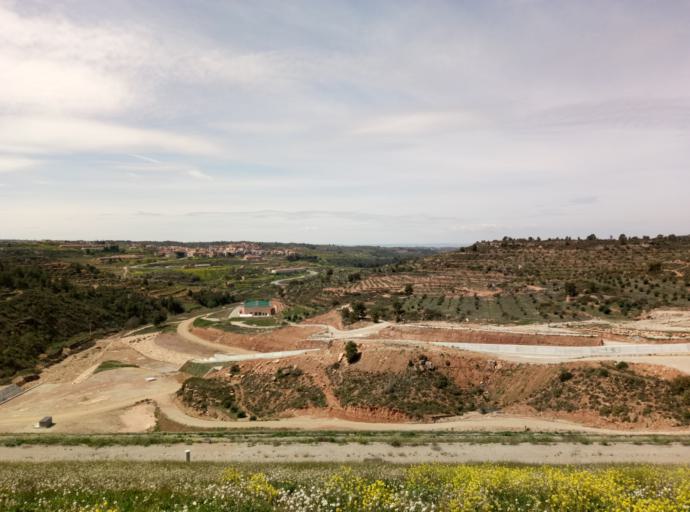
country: ES
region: Catalonia
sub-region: Provincia de Lleida
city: el Cogul
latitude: 41.4523
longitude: 0.7583
